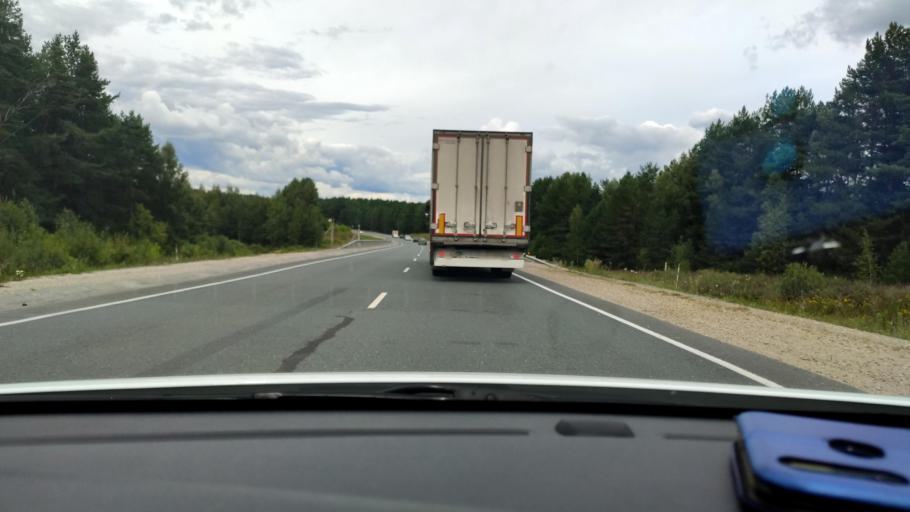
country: RU
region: Mariy-El
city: Pomary
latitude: 55.9957
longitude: 48.3821
